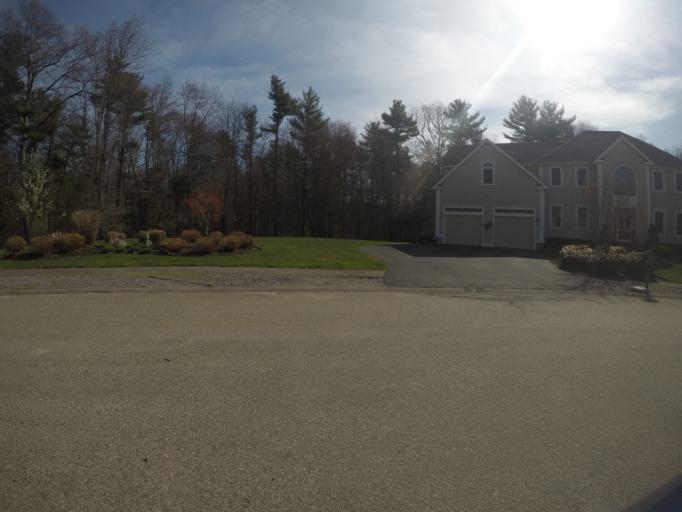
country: US
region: Massachusetts
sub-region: Bristol County
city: Easton
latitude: 42.0186
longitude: -71.1193
